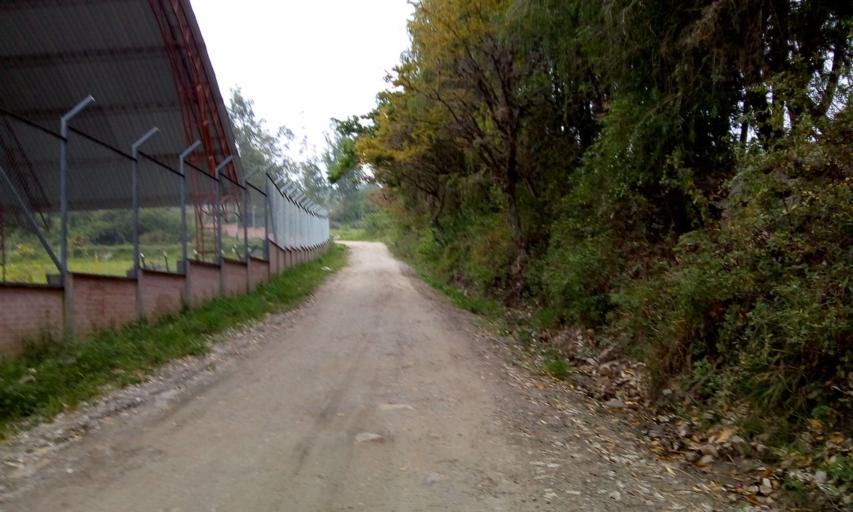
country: CO
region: Boyaca
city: Tipacoque
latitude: 6.4130
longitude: -72.6878
